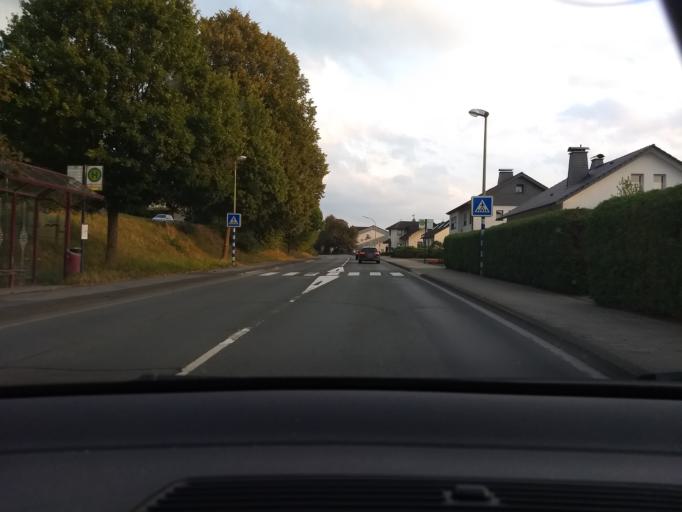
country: DE
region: North Rhine-Westphalia
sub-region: Regierungsbezirk Arnsberg
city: Arnsberg
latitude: 51.3621
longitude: 8.1703
